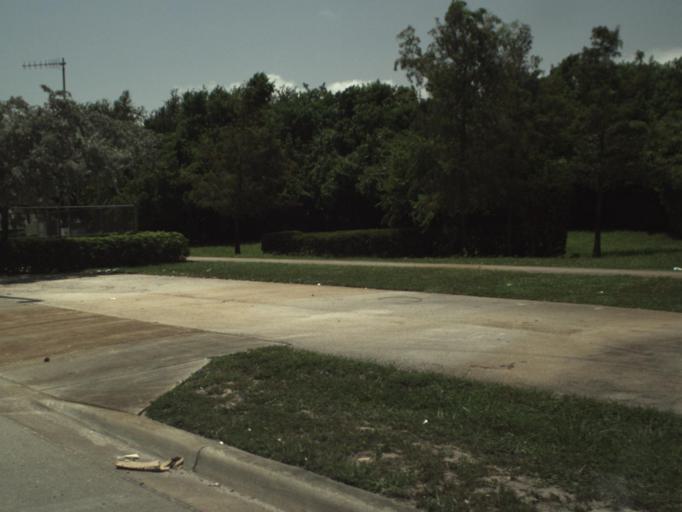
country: US
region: Florida
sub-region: Broward County
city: Coconut Creek
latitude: 26.2590
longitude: -80.1520
